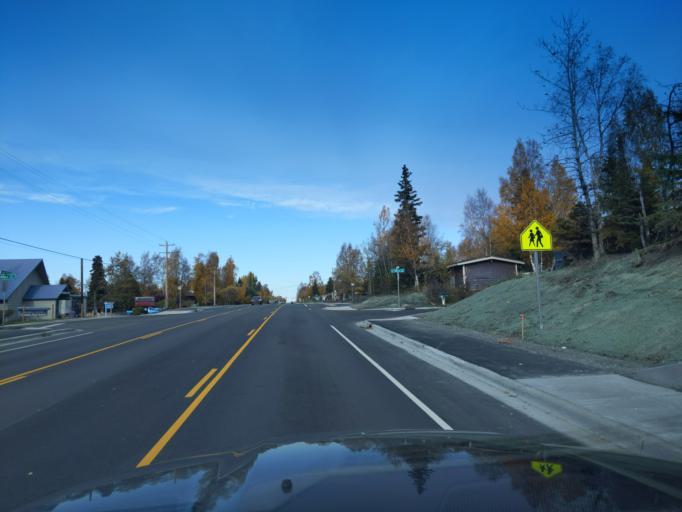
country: US
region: Alaska
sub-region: Anchorage Municipality
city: Anchorage
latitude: 61.1461
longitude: -149.9518
